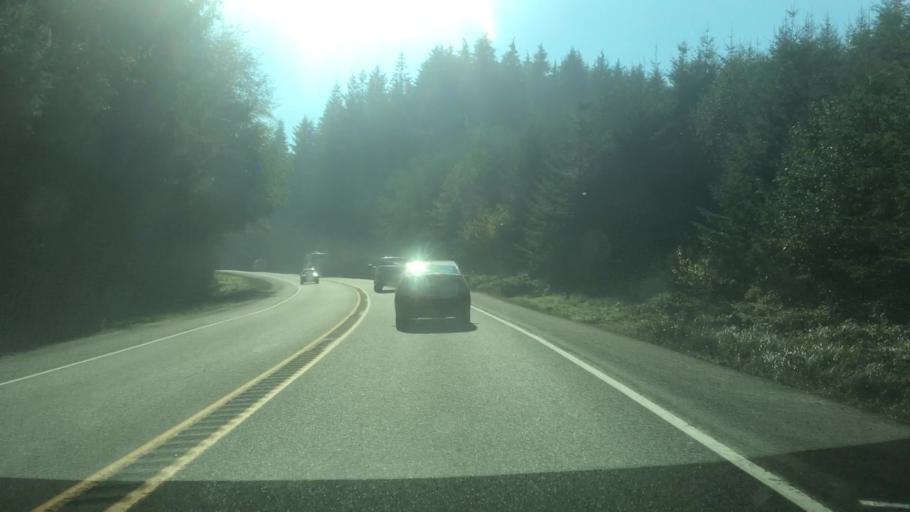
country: US
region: Washington
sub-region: Grays Harbor County
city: Central Park
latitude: 46.9275
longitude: -123.7157
